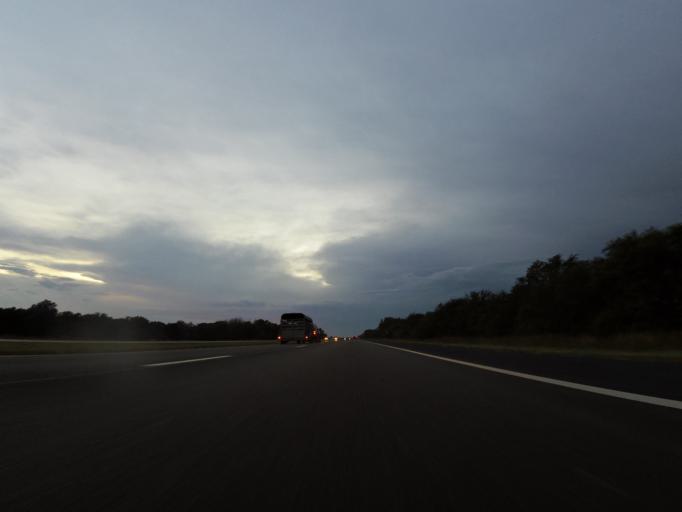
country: US
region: Kansas
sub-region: Reno County
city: Haven
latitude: 37.8846
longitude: -97.7298
